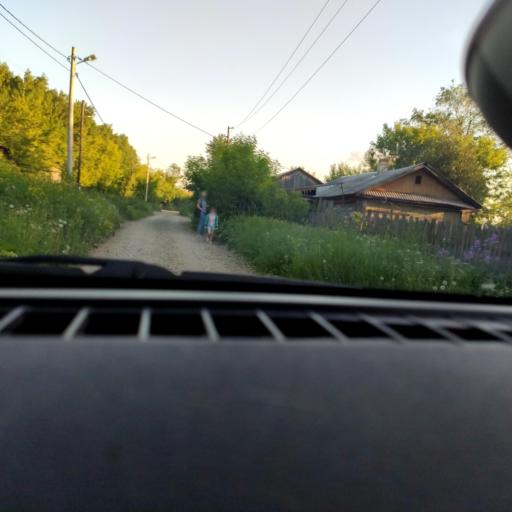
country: RU
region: Perm
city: Polazna
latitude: 58.1383
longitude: 56.3805
